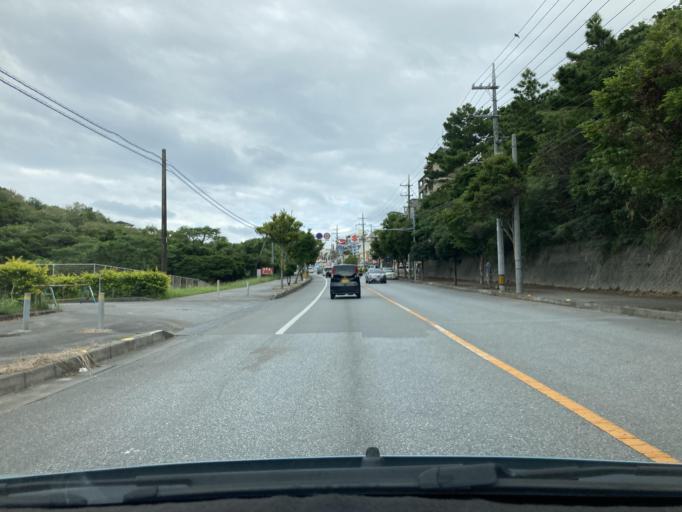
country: JP
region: Okinawa
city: Ginowan
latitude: 26.2458
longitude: 127.7598
